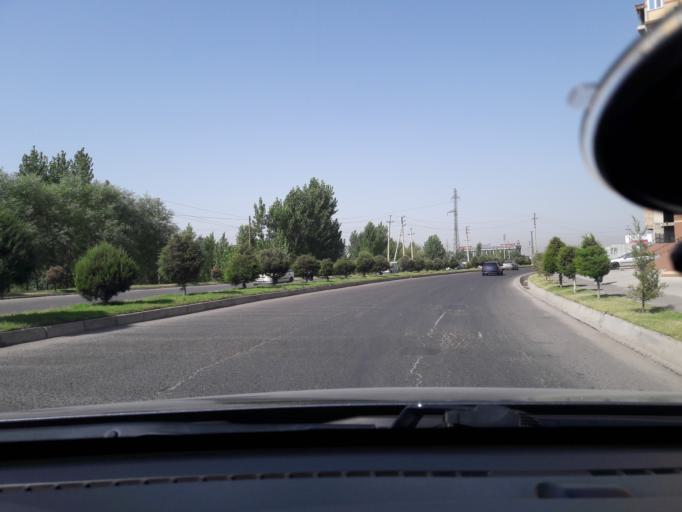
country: TJ
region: Dushanbe
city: Dushanbe
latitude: 38.5012
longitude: 68.7597
